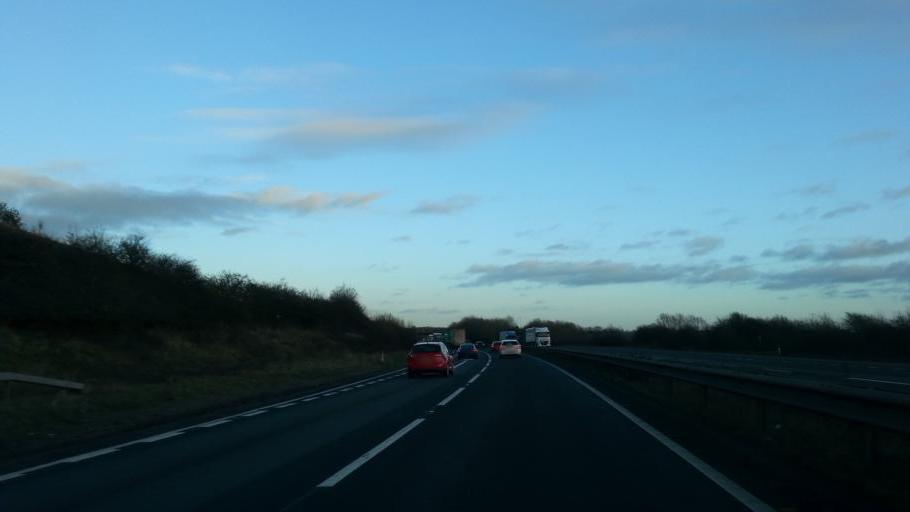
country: GB
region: England
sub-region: Northamptonshire
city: Thrapston
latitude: 52.3908
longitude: -0.5639
